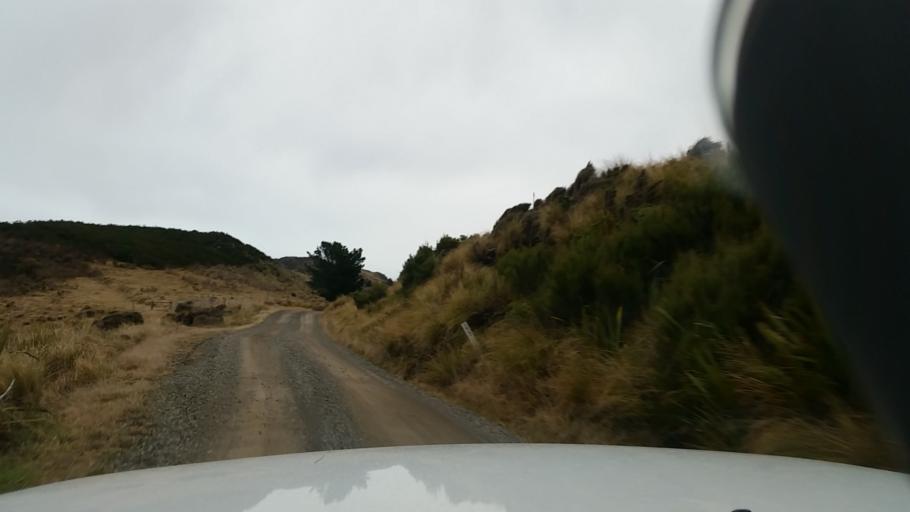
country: NZ
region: Canterbury
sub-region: Christchurch City
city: Christchurch
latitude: -43.8080
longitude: 172.8474
